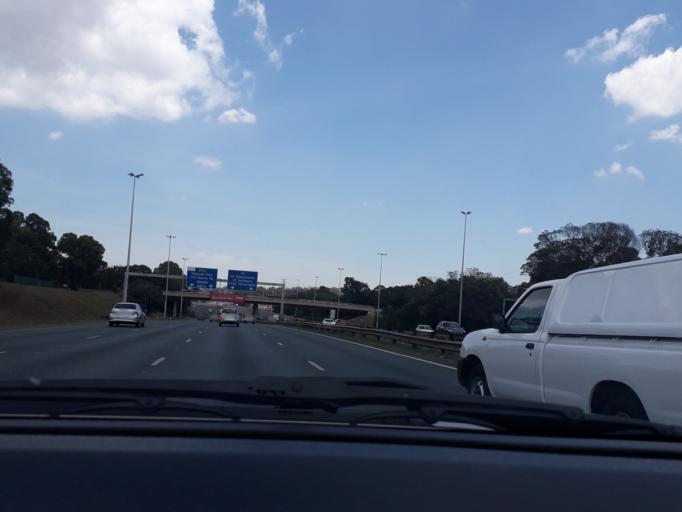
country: ZA
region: Gauteng
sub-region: City of Johannesburg Metropolitan Municipality
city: Johannesburg
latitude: -26.2509
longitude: 27.9976
